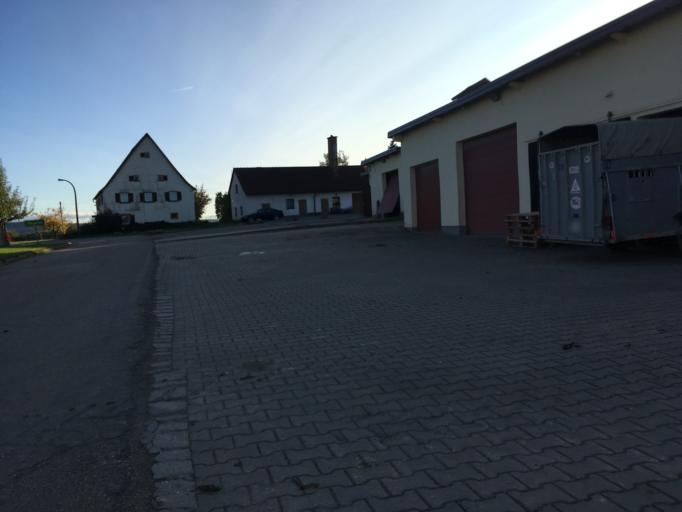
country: DE
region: Baden-Wuerttemberg
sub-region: Regierungsbezirk Stuttgart
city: Neuenstein
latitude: 49.2292
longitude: 9.6109
